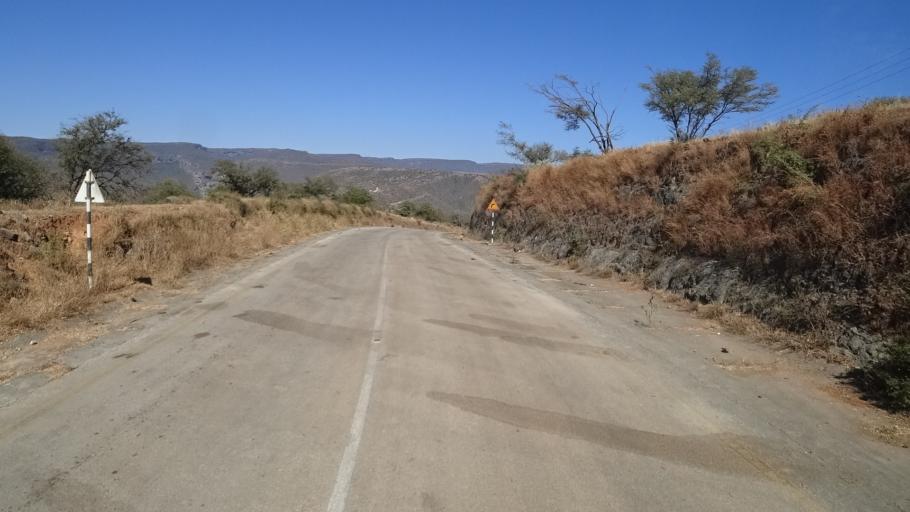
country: YE
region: Al Mahrah
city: Hawf
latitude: 16.7451
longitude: 53.3953
